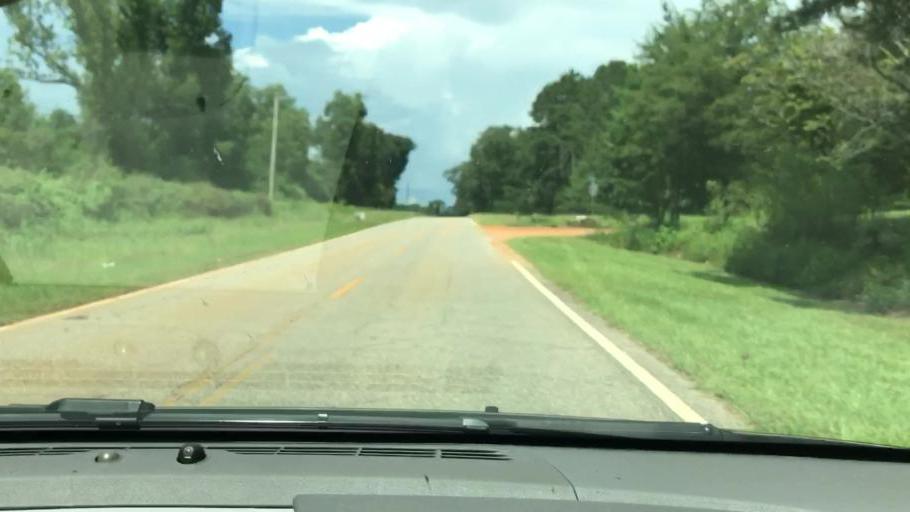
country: US
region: Georgia
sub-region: Early County
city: Blakely
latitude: 31.2249
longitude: -84.9964
